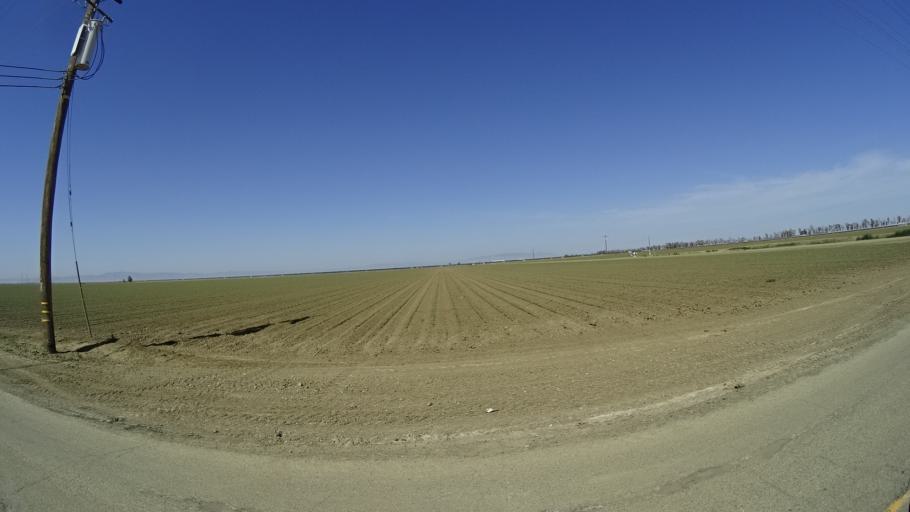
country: US
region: California
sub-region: Kings County
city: Lemoore Station
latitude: 36.2474
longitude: -119.9053
